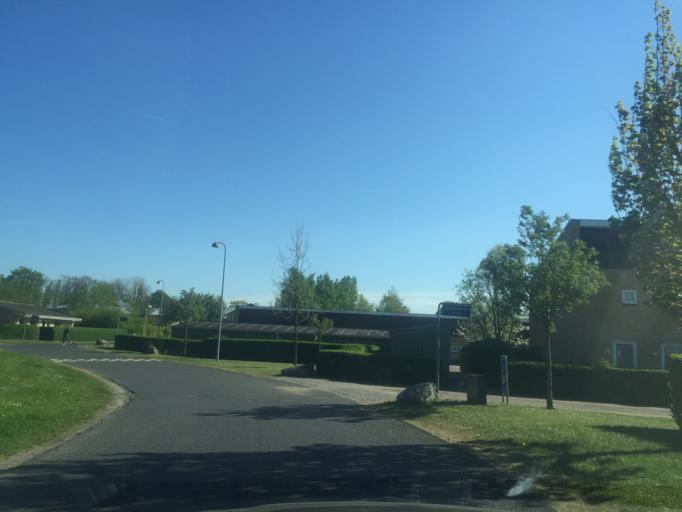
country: DK
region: South Denmark
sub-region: Odense Kommune
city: Odense
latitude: 55.3691
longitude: 10.4065
